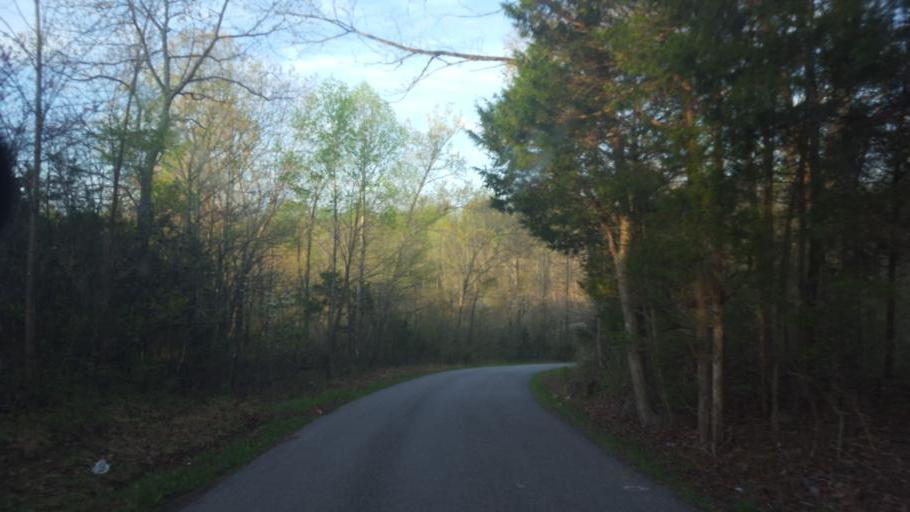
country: US
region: Kentucky
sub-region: Barren County
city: Cave City
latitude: 37.1748
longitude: -86.0002
